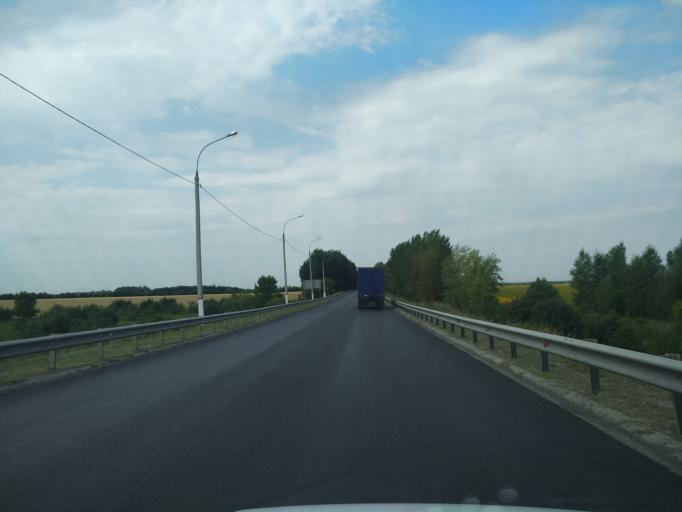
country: RU
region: Voronezj
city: Pereleshino
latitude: 51.7590
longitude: 40.1214
